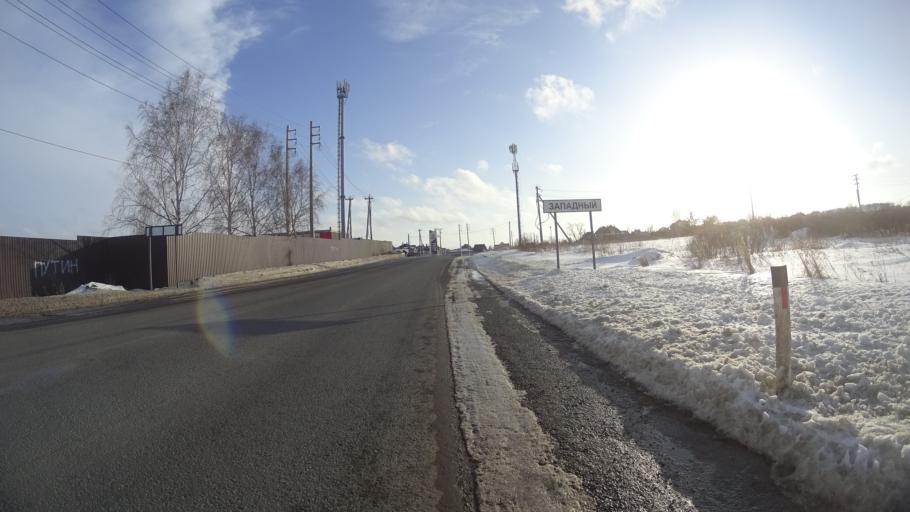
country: RU
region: Chelyabinsk
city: Sargazy
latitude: 55.1192
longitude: 61.2865
